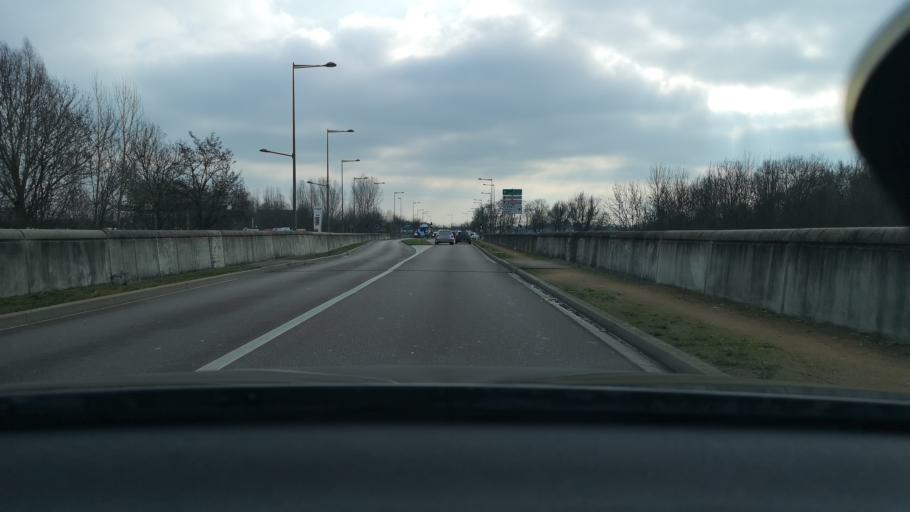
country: FR
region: Bourgogne
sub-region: Departement de Saone-et-Loire
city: Saint-Remy
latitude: 46.7762
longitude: 4.8354
